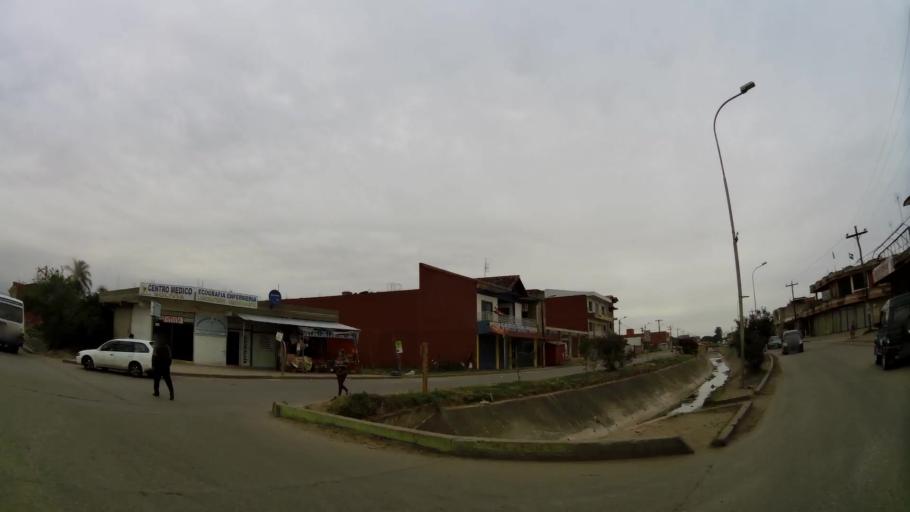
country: BO
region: Santa Cruz
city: Santa Cruz de la Sierra
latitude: -17.8545
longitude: -63.1636
